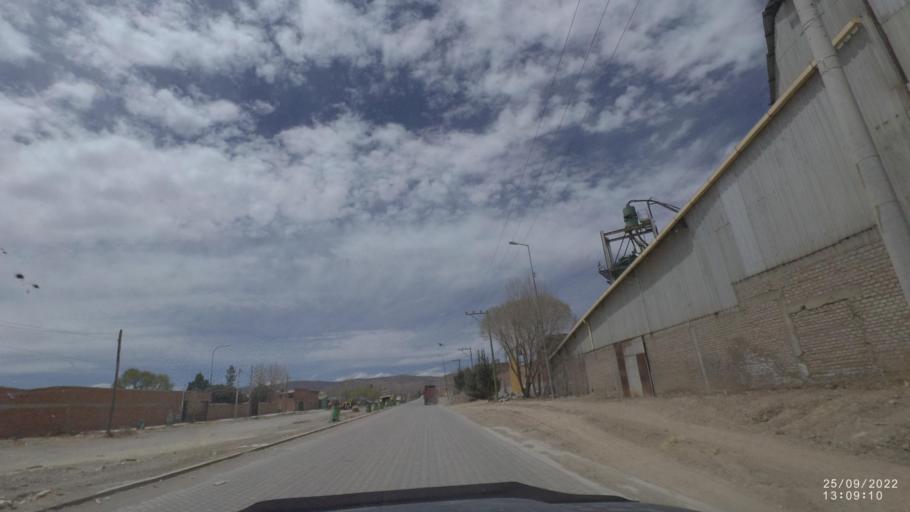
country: BO
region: Oruro
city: Oruro
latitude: -17.9763
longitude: -67.0583
